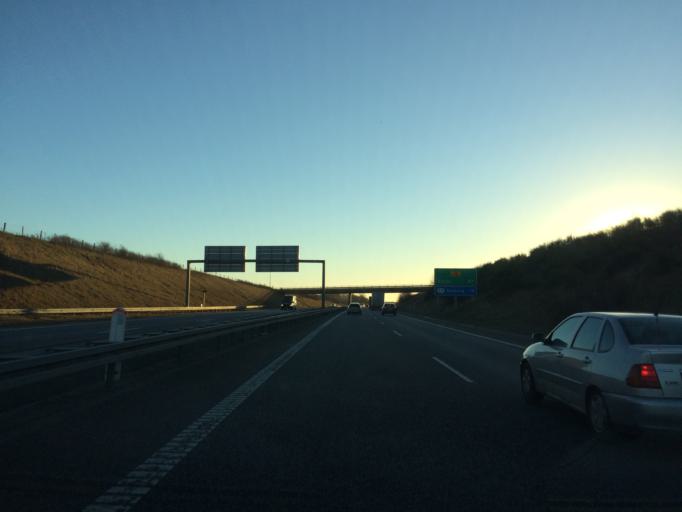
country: DK
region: Central Jutland
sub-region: Herning Kommune
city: Lind
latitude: 56.1024
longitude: 9.0074
